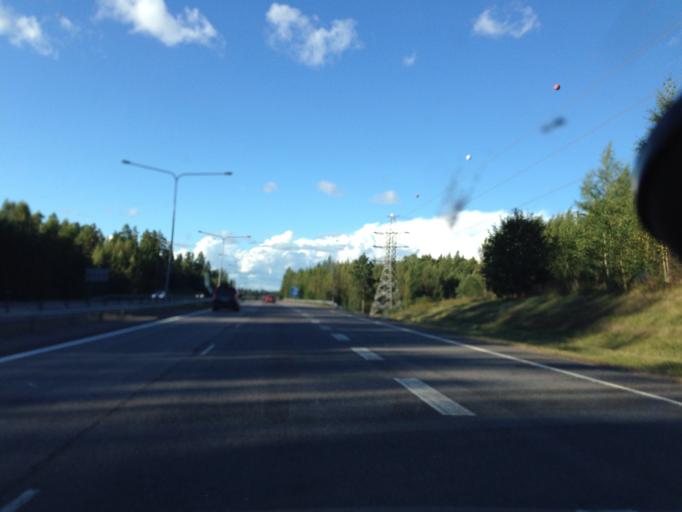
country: FI
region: Uusimaa
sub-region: Helsinki
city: Vantaa
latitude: 60.3275
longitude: 24.9986
